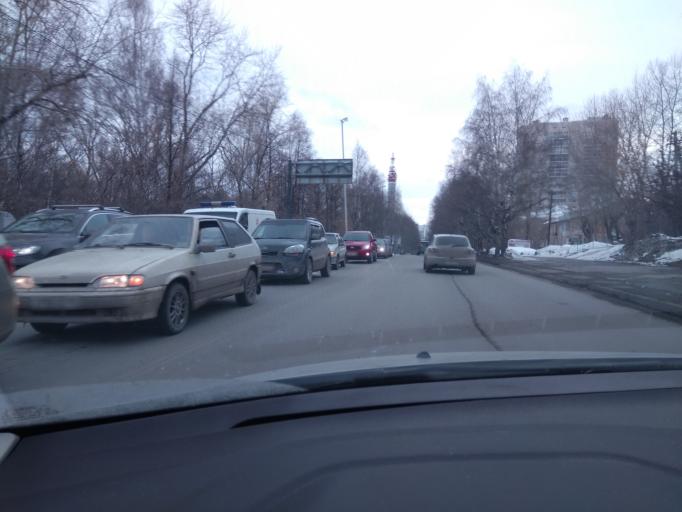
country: RU
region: Sverdlovsk
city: Yekaterinburg
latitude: 56.8511
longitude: 60.6406
